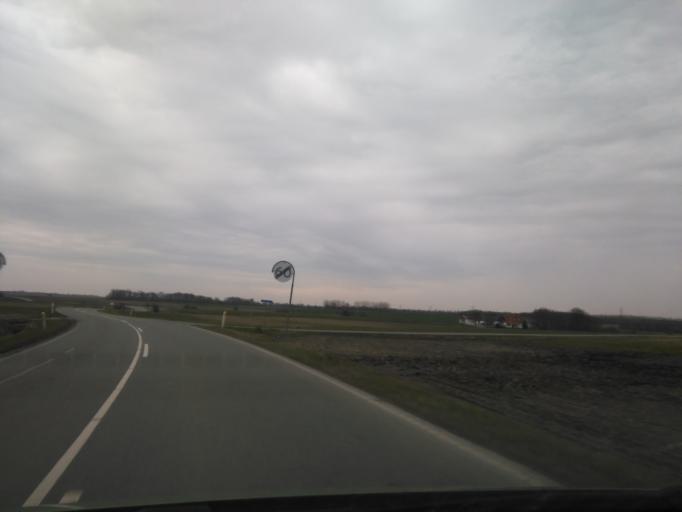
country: DK
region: Central Jutland
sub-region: Randers Kommune
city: Spentrup
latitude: 56.5360
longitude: 9.9993
